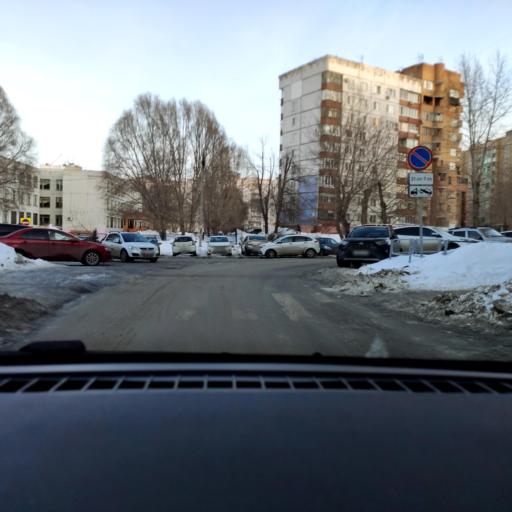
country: RU
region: Samara
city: Novokuybyshevsk
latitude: 53.1059
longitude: 49.9513
